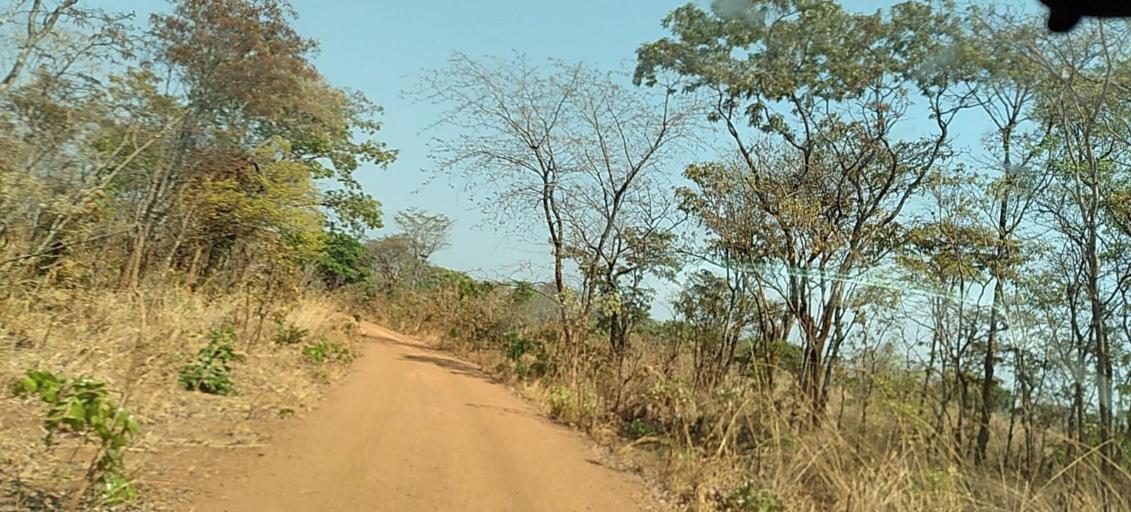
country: ZM
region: North-Western
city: Kasempa
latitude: -13.3897
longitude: 25.6839
